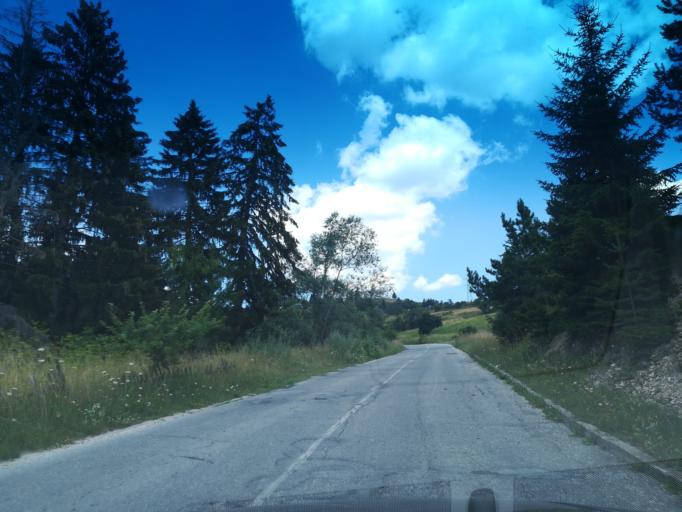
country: BG
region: Smolyan
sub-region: Obshtina Chepelare
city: Chepelare
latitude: 41.6681
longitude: 24.7739
